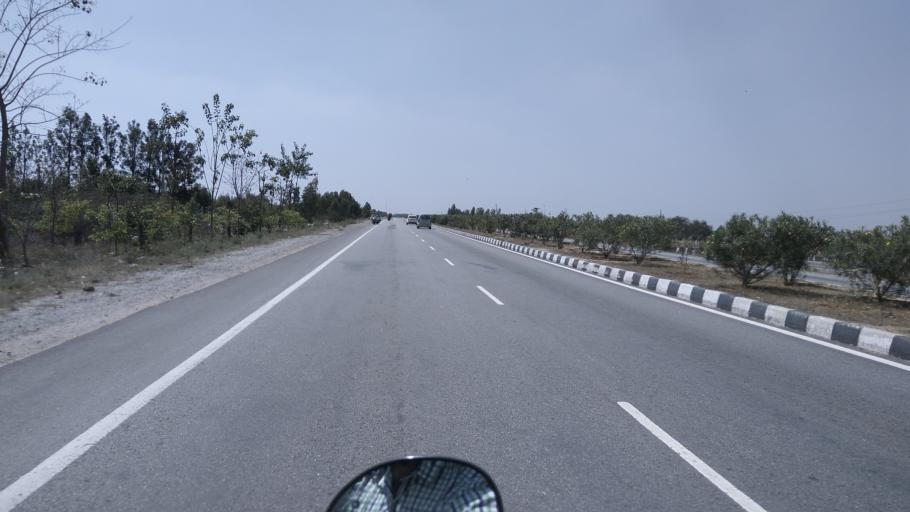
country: IN
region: Karnataka
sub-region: Kolar
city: Mulbagal
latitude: 13.1522
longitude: 78.3823
